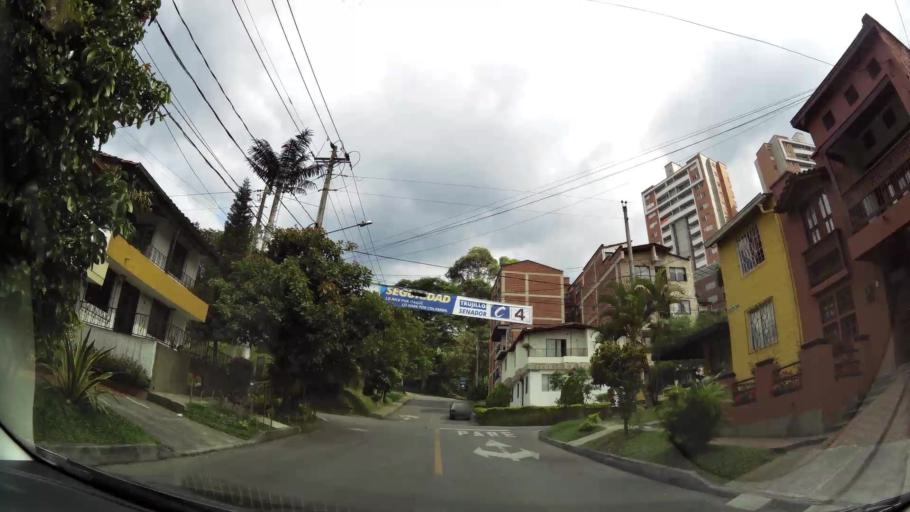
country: CO
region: Antioquia
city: Envigado
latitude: 6.1577
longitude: -75.5923
